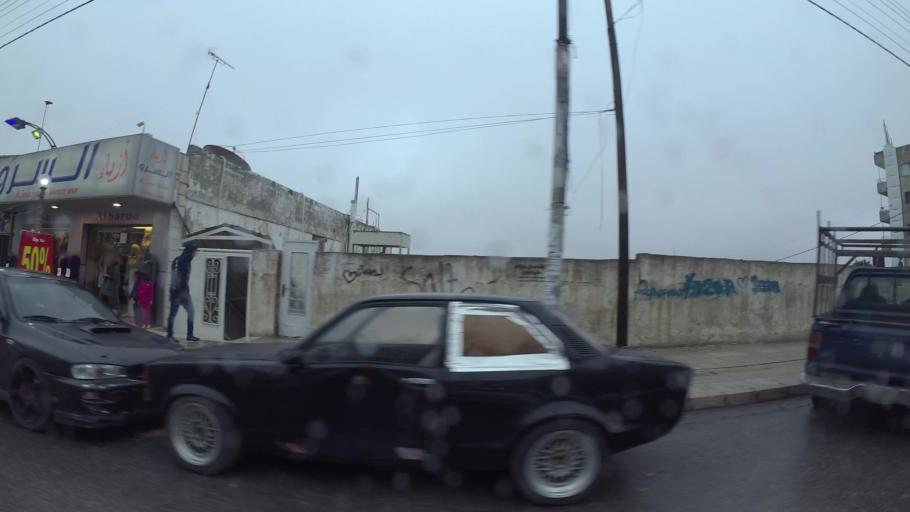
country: JO
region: Amman
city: Al Jubayhah
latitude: 32.0238
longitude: 35.8392
